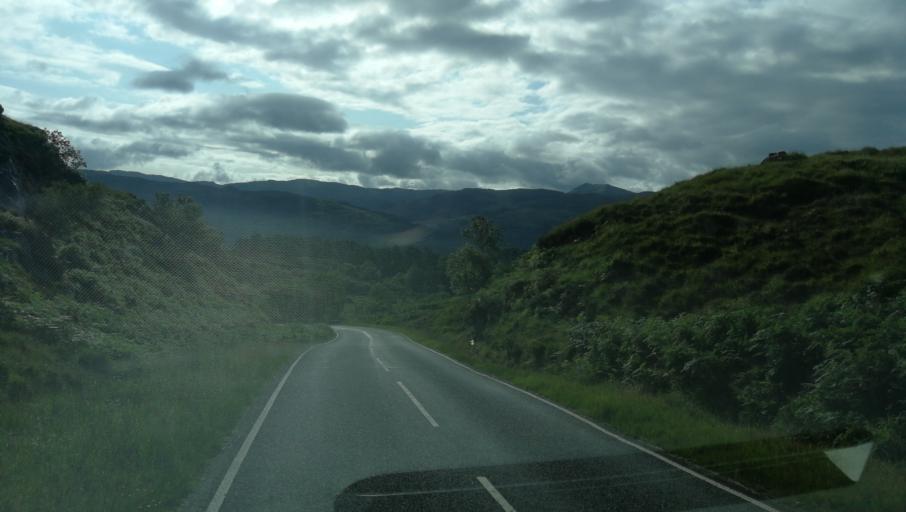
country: GB
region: Scotland
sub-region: Argyll and Bute
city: Isle Of Mull
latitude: 56.6787
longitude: -5.8468
